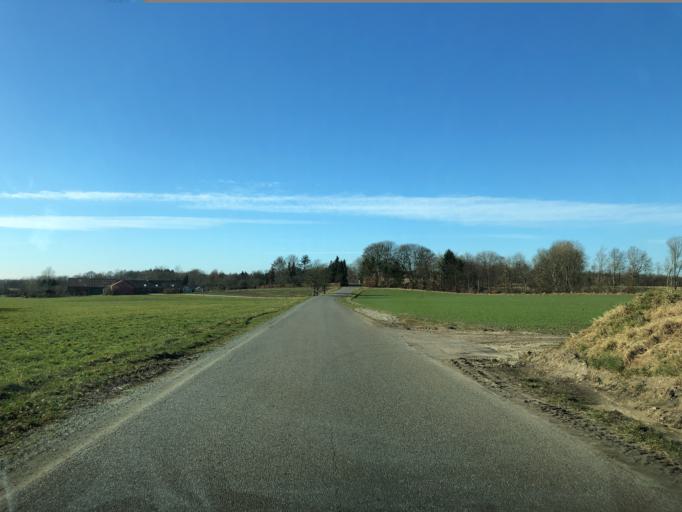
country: DK
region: Central Jutland
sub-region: Ikast-Brande Kommune
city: Bording Kirkeby
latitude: 56.1555
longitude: 9.2396
